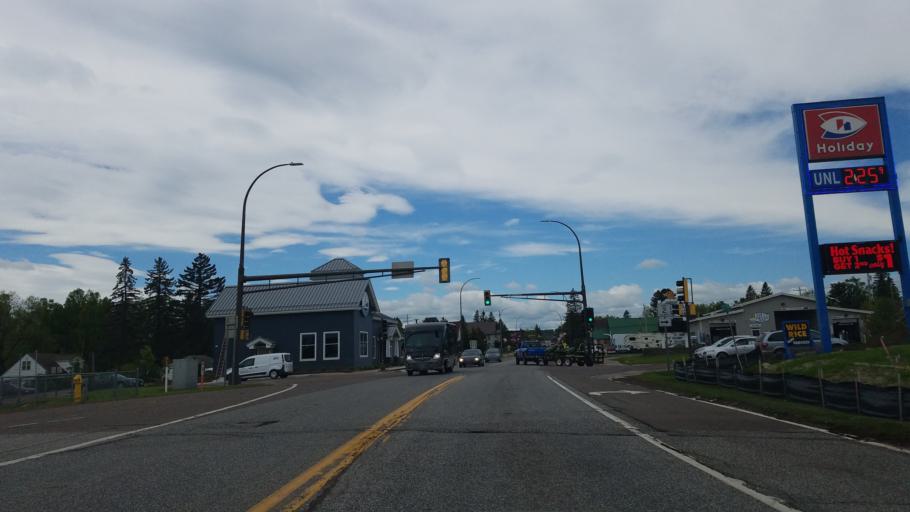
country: US
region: Minnesota
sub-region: Lake County
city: Two Harbors
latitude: 47.0258
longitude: -91.6665
